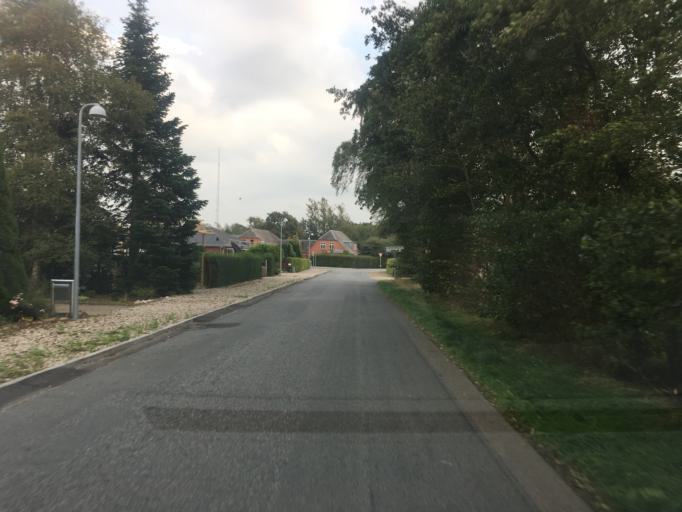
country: DE
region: Schleswig-Holstein
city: Bramstedtlund
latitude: 54.9500
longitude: 9.0977
